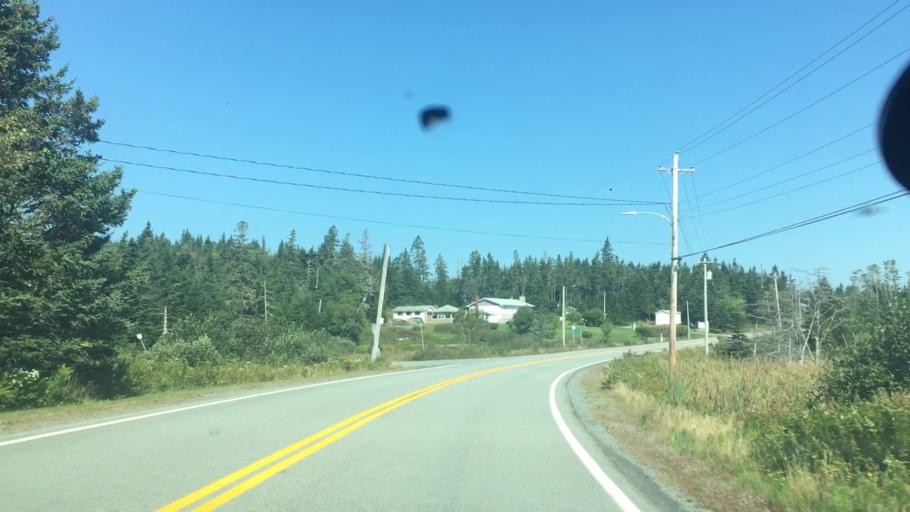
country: CA
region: Nova Scotia
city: New Glasgow
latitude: 44.9267
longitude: -62.2984
